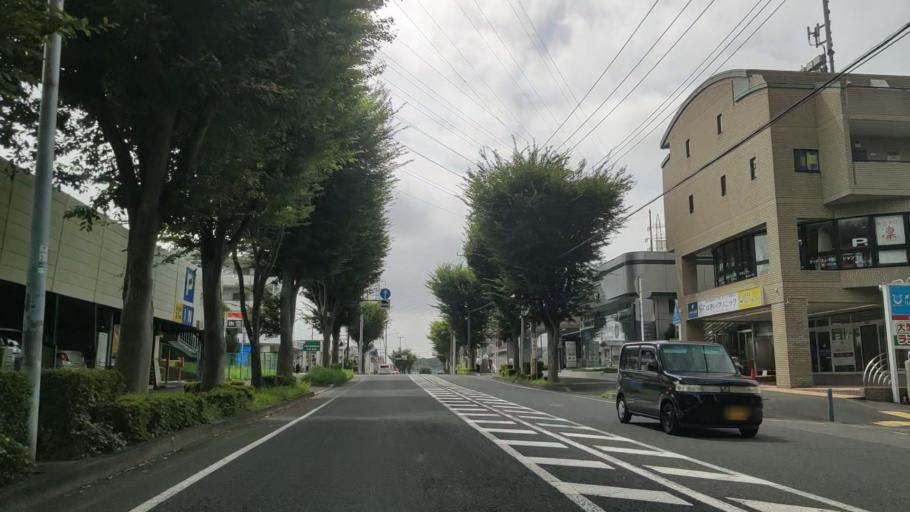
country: JP
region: Kanagawa
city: Fujisawa
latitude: 35.4170
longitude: 139.5229
